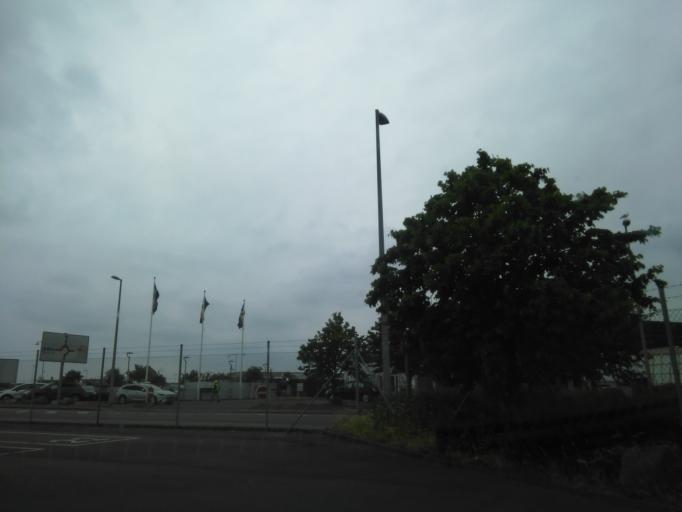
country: DK
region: Capital Region
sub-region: Bornholm Kommune
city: Ronne
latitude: 55.1007
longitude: 14.6910
